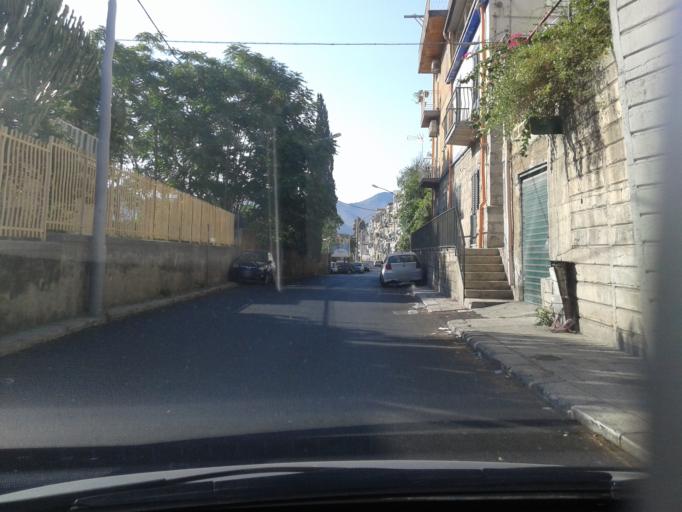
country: IT
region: Sicily
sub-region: Palermo
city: Piano dei Geli
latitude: 38.1090
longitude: 13.3086
